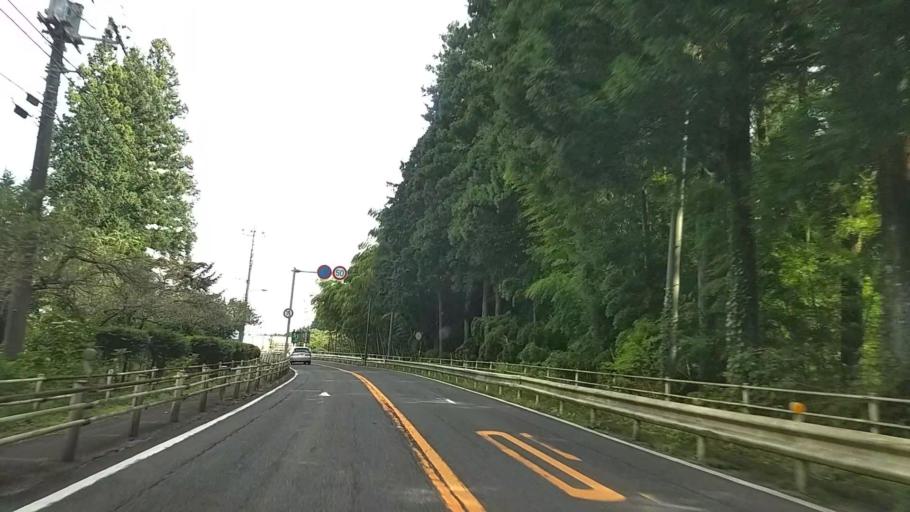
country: JP
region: Tochigi
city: Imaichi
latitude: 36.7288
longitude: 139.6699
